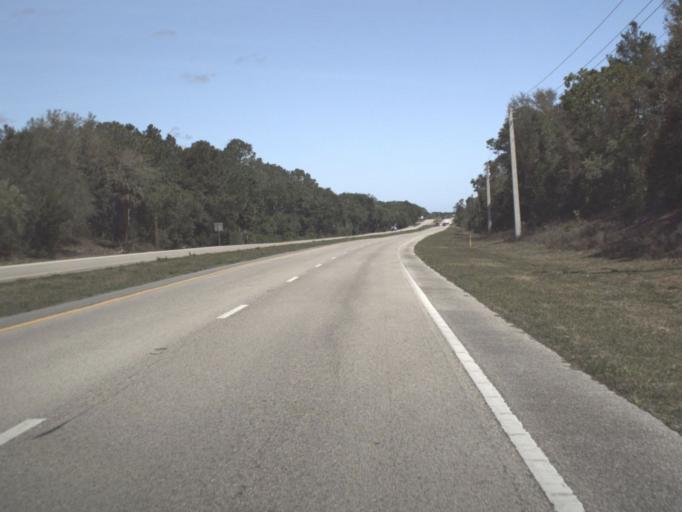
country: US
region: Florida
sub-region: Flagler County
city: Palm Coast
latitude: 29.6456
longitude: -81.2862
